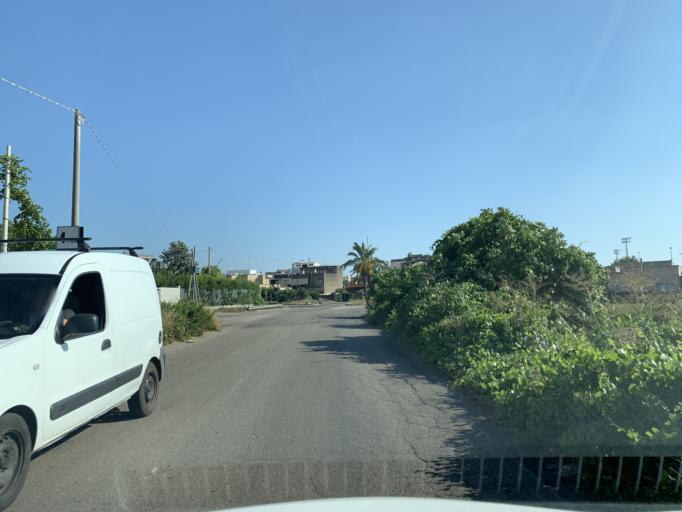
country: IT
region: Apulia
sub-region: Provincia di Lecce
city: Nardo
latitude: 40.1860
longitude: 18.0390
